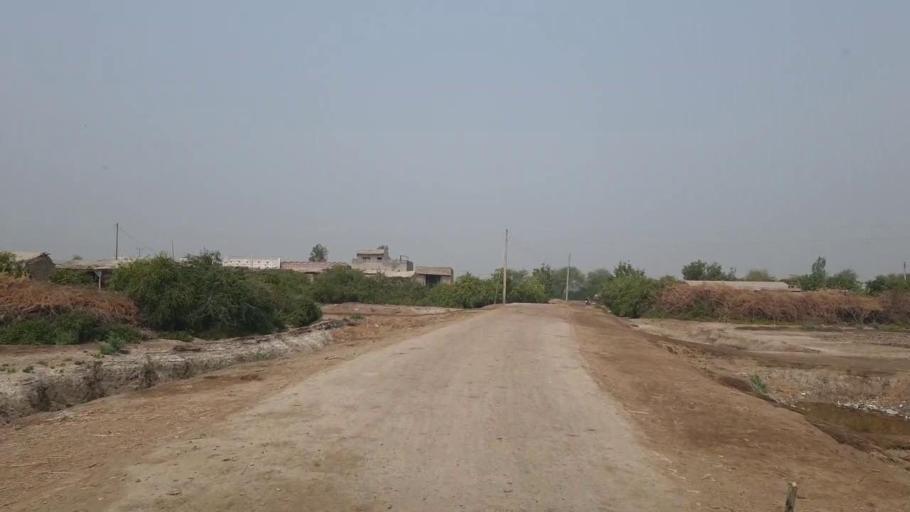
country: PK
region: Sindh
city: Kario
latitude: 24.6593
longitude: 68.6205
